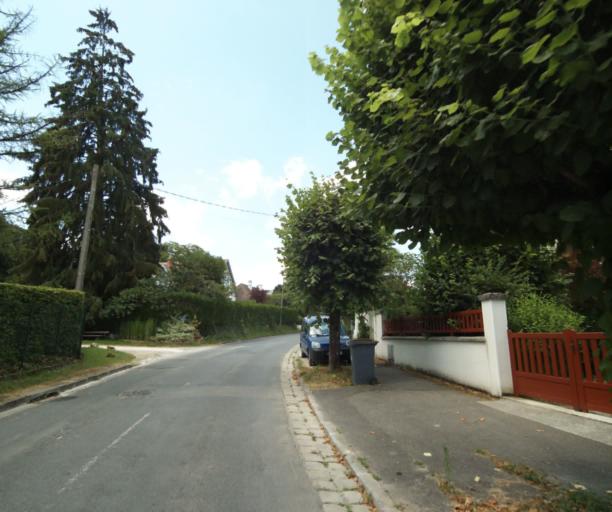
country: FR
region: Ile-de-France
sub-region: Departement de Seine-et-Marne
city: Samois-sur-Seine
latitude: 48.4533
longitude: 2.7550
